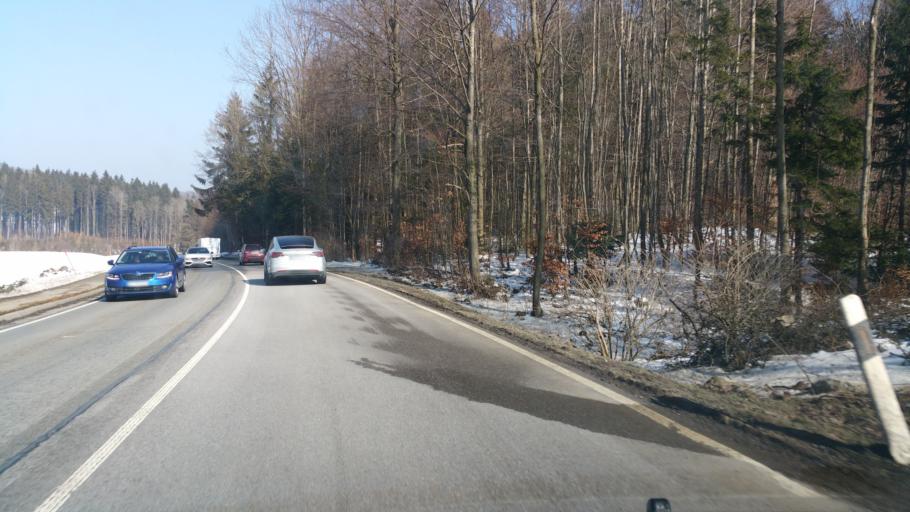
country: DE
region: Bavaria
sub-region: Upper Bavaria
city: Miesbach
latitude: 47.8023
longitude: 11.8537
